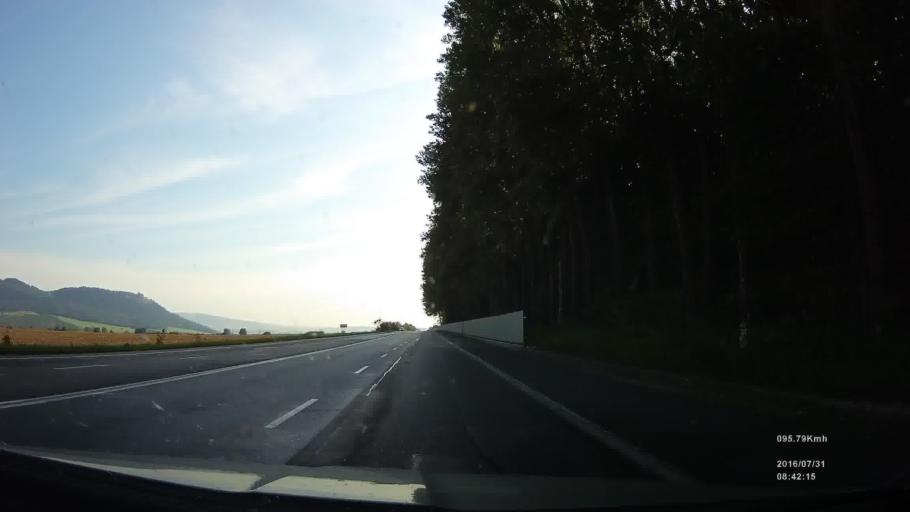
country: SK
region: Presovsky
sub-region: Okres Presov
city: Presov
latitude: 49.0285
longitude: 21.2950
